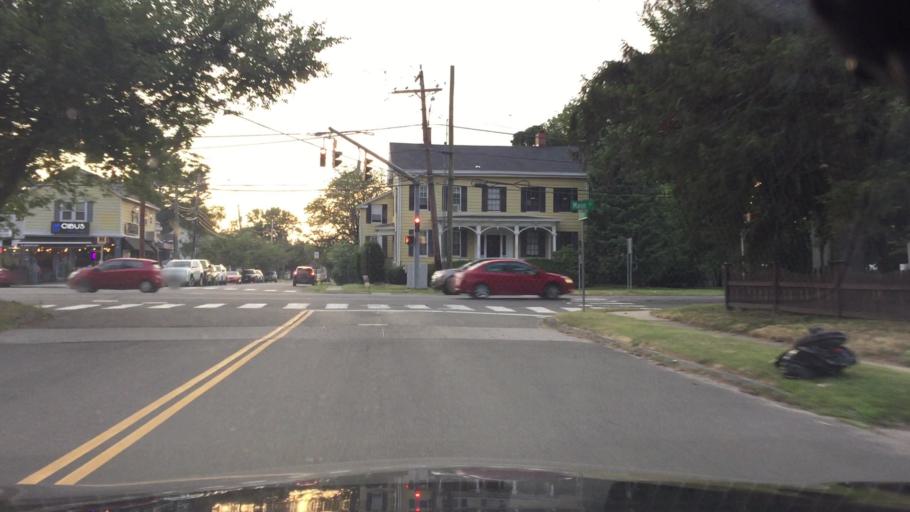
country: US
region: Connecticut
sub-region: Fairfield County
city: Stratford
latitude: 41.1795
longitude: -73.1299
